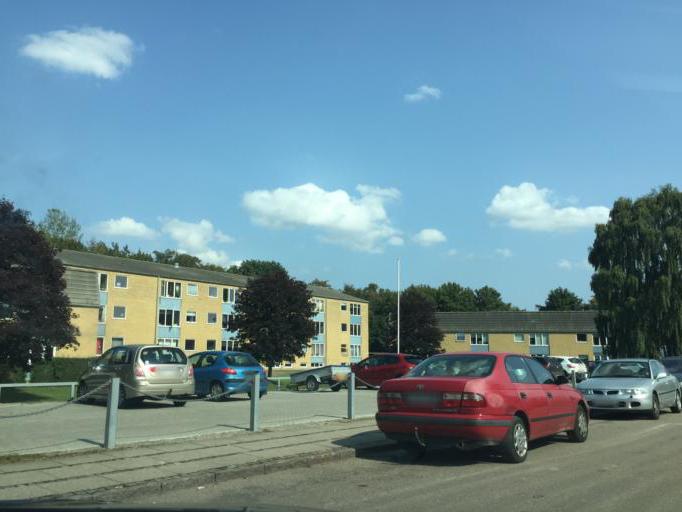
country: DK
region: South Denmark
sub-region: Odense Kommune
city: Odense
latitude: 55.4018
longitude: 10.3435
